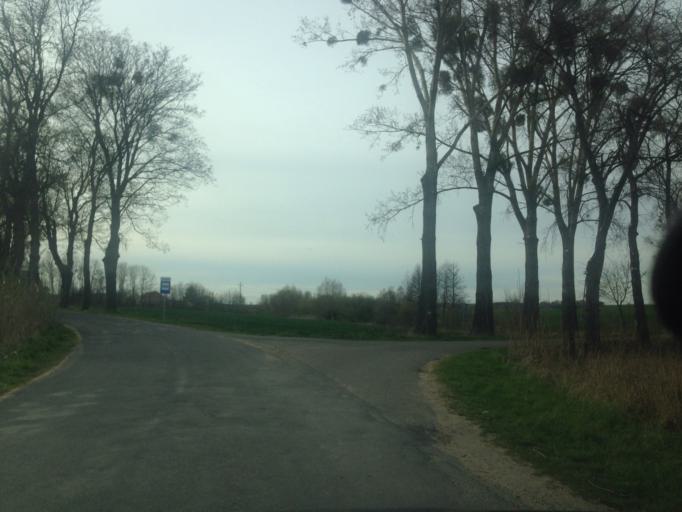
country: PL
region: Kujawsko-Pomorskie
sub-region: Powiat grudziadzki
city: Swiecie nad Osa
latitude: 53.4757
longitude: 19.1566
